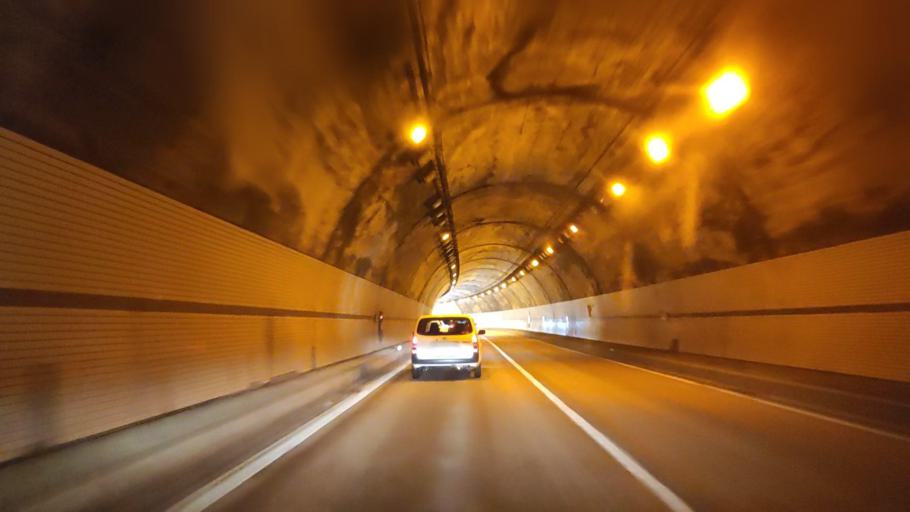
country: JP
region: Toyama
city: Yatsuomachi-higashikumisaka
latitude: 36.5033
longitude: 137.2331
